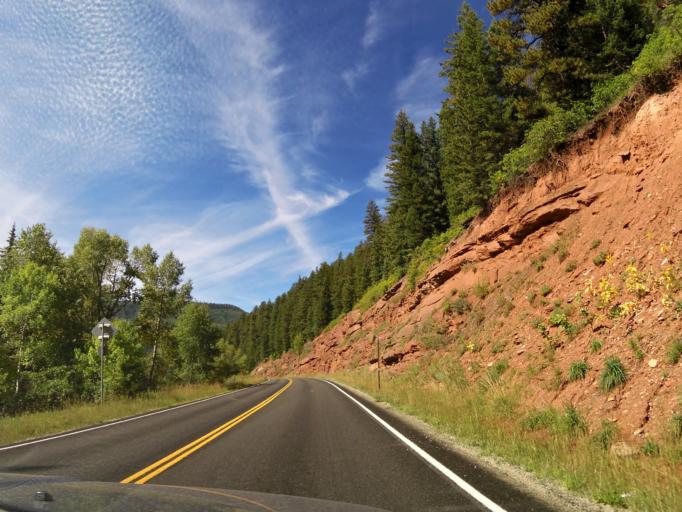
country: US
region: Colorado
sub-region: Montezuma County
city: Mancos
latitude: 37.5816
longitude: -108.1744
